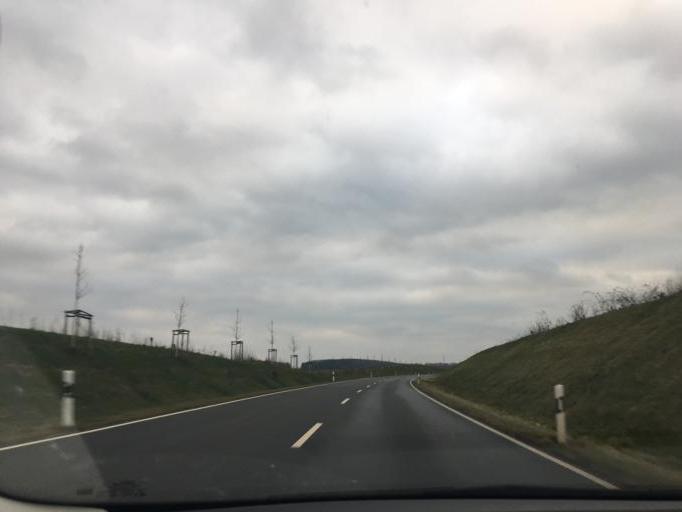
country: DE
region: Saxony
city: Niederfrohna
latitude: 50.8964
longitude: 12.7168
